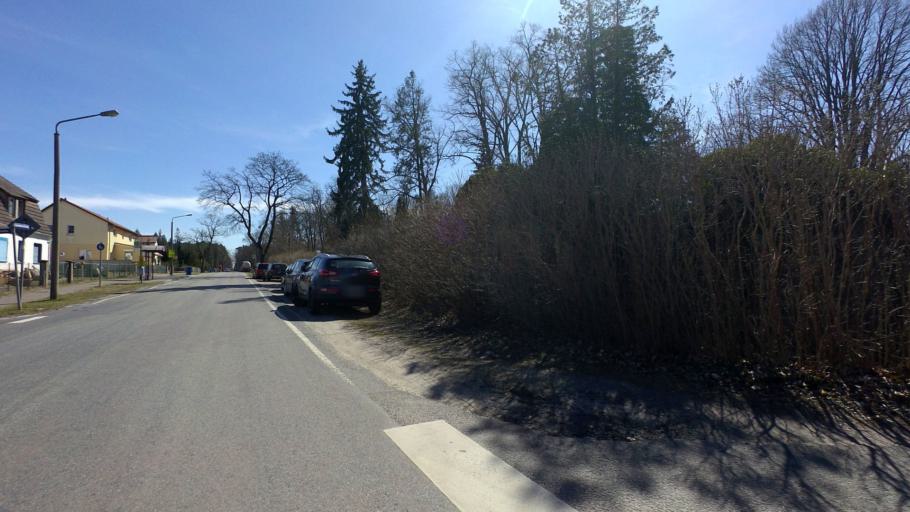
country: DE
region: Brandenburg
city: Teupitz
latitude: 52.1317
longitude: 13.6207
